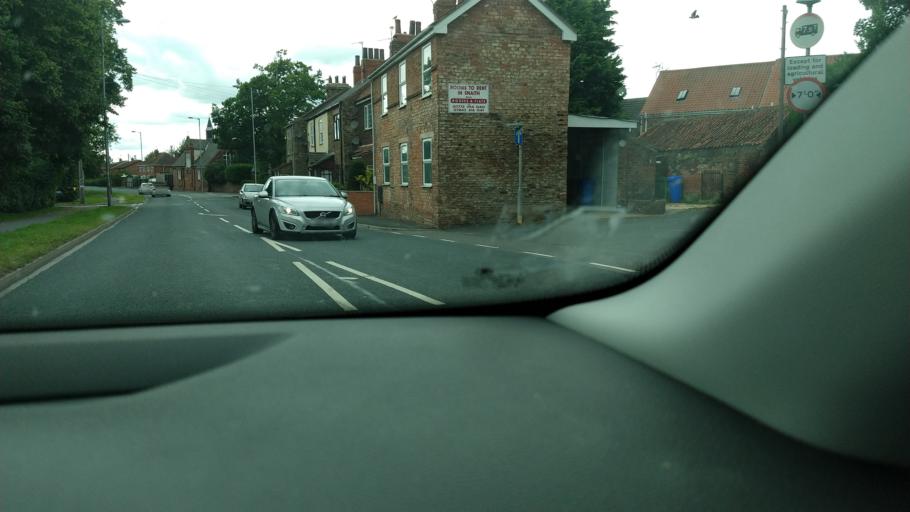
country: GB
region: England
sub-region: East Riding of Yorkshire
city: Snaith
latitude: 53.6904
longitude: -1.0316
